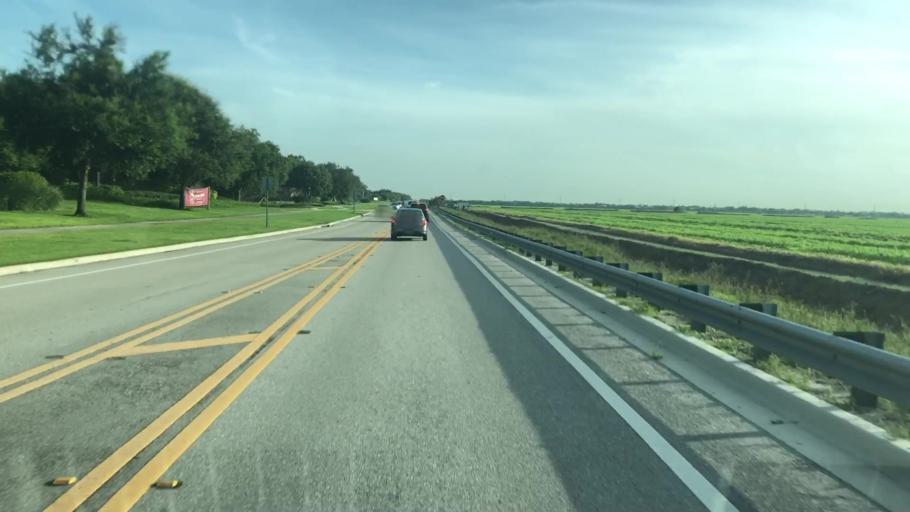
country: US
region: Florida
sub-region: Broward County
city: Parkland
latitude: 26.3221
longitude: -80.2508
